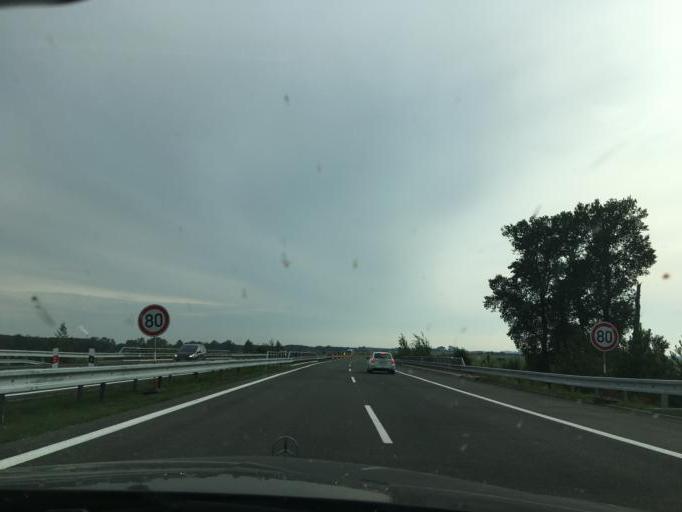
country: CZ
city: Stezery
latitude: 50.1788
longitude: 15.7632
